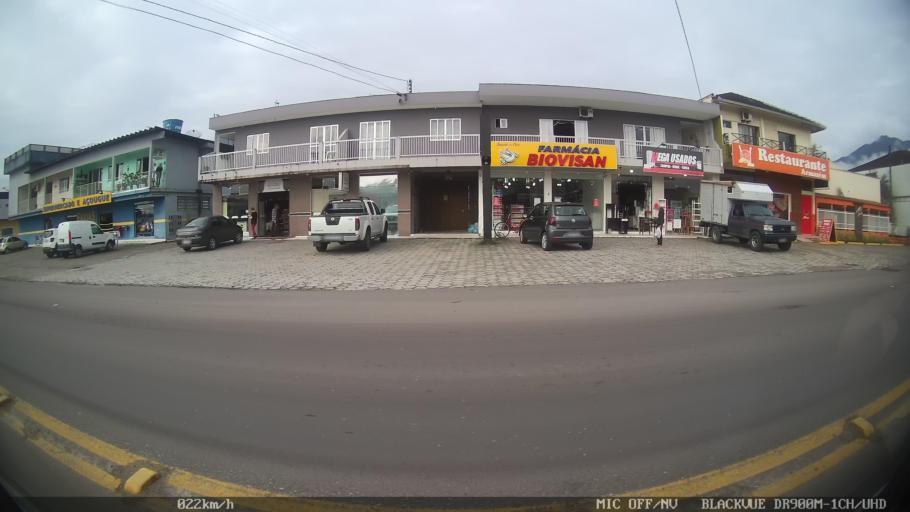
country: BR
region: Santa Catarina
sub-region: Joinville
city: Joinville
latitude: -26.0298
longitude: -48.8535
